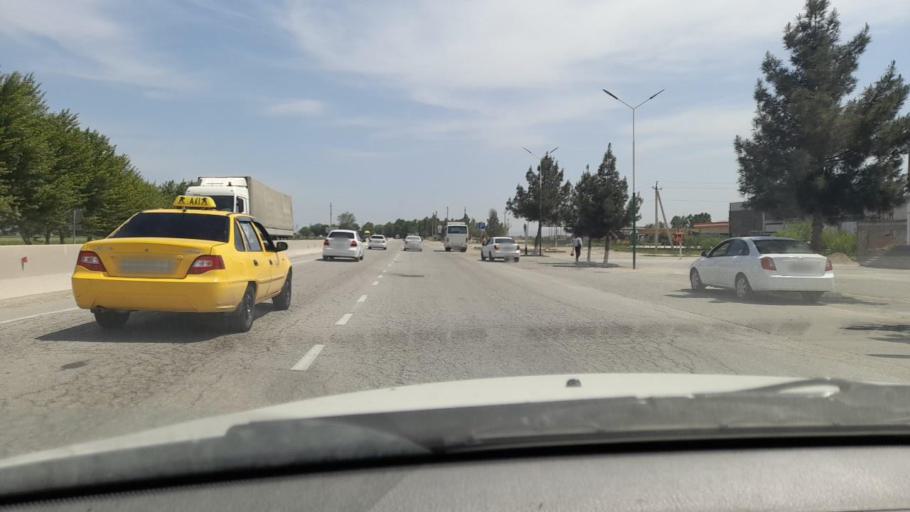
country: UZ
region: Navoiy
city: Karmana Shahri
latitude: 40.1298
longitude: 65.4117
